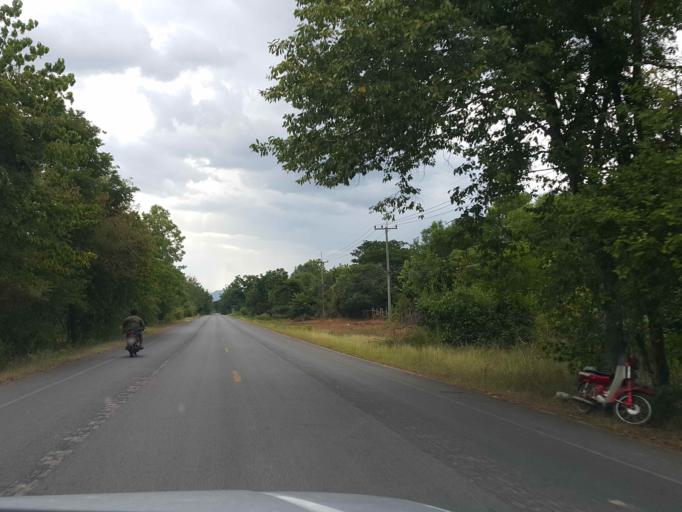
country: TH
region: Lampang
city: Thoen
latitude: 17.6497
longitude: 99.2713
